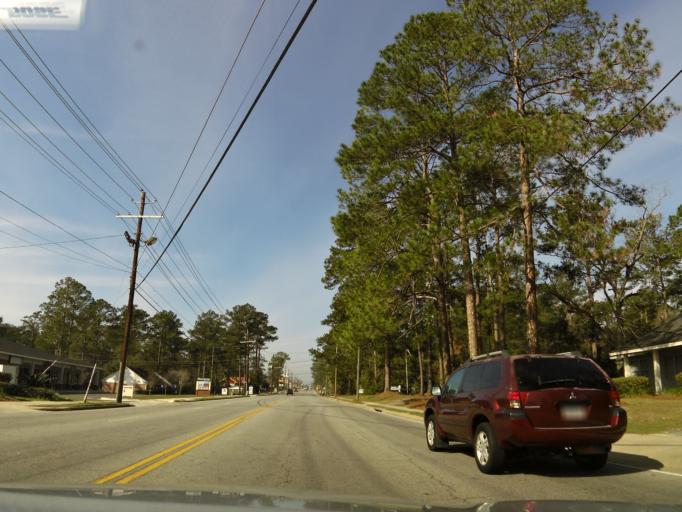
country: US
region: Georgia
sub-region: Lowndes County
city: Remerton
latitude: 30.8468
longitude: -83.2981
